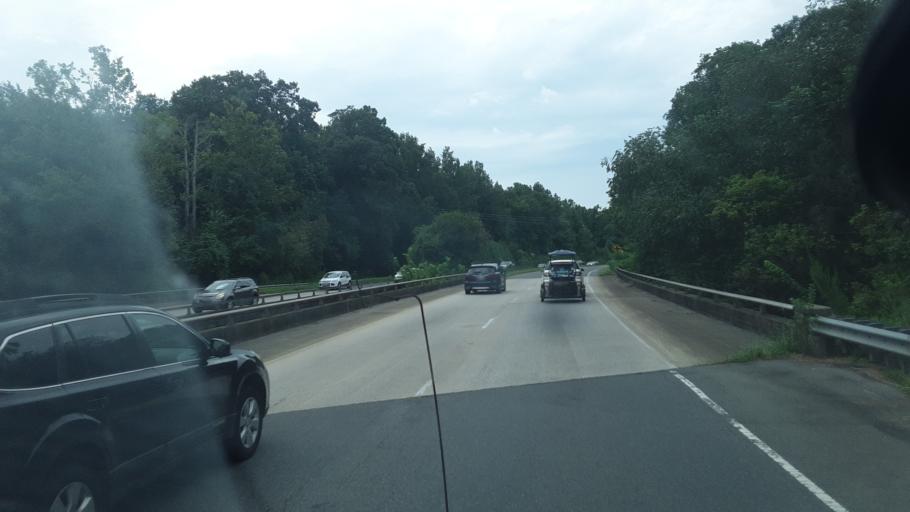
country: US
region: North Carolina
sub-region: Richmond County
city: Rockingham
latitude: 34.9463
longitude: -79.7754
